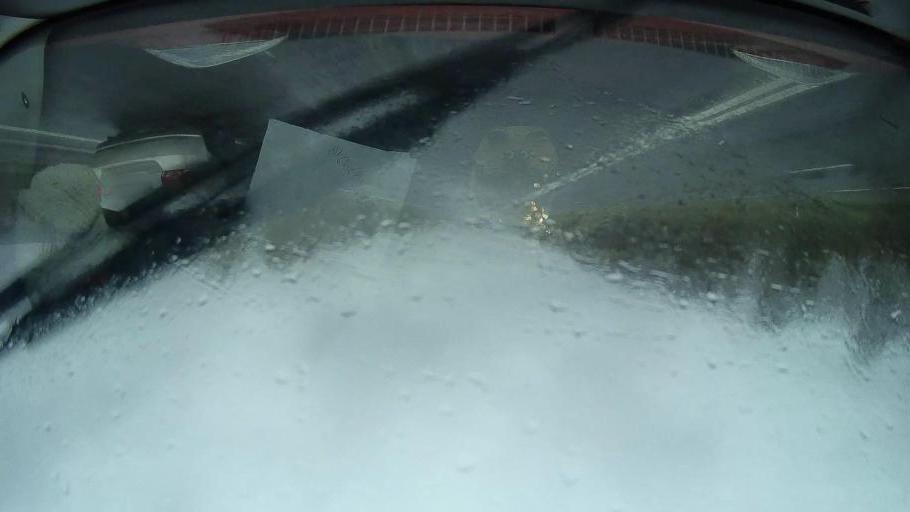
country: RU
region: Stavropol'skiy
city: Nevinnomyssk
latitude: 44.6199
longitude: 42.0920
